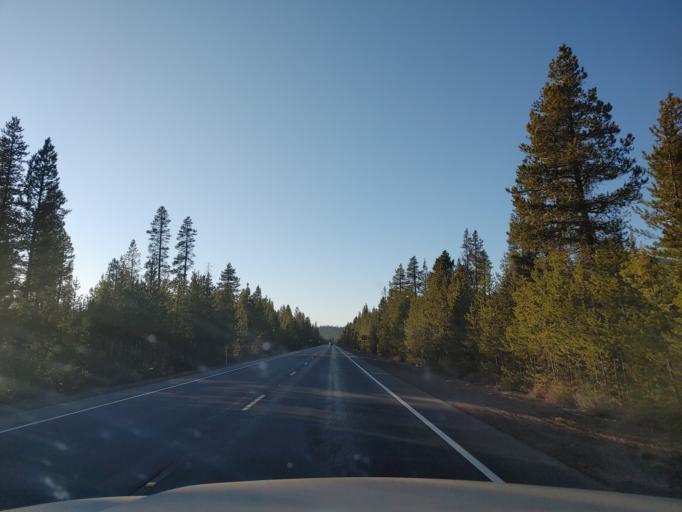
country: US
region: Oregon
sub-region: Deschutes County
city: La Pine
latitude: 43.4288
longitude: -121.8510
